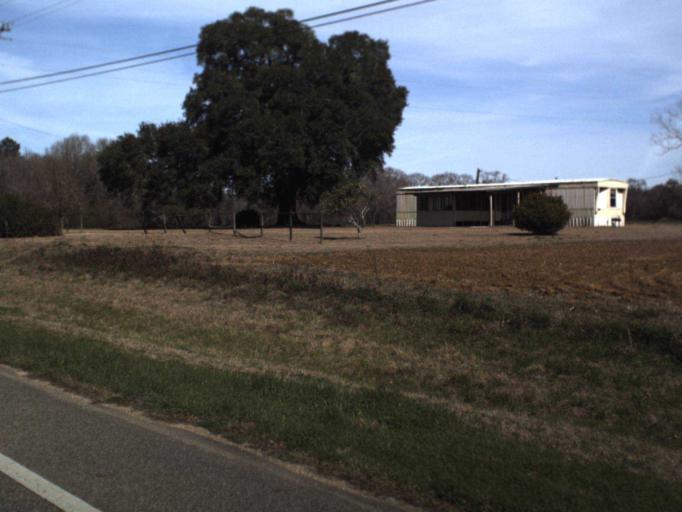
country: US
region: Florida
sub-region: Washington County
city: Chipley
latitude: 30.8527
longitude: -85.5287
